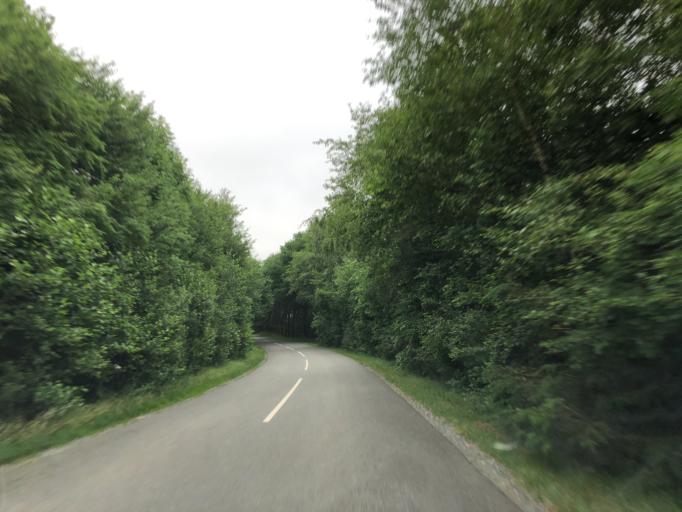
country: DK
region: Central Jutland
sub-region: Holstebro Kommune
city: Holstebro
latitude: 56.2528
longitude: 8.6275
